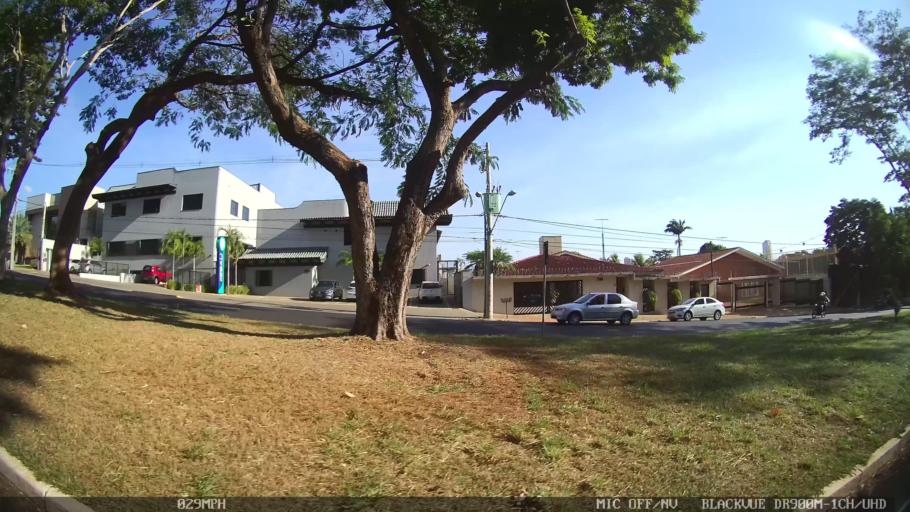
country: BR
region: Sao Paulo
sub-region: Ribeirao Preto
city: Ribeirao Preto
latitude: -21.1990
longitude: -47.7920
